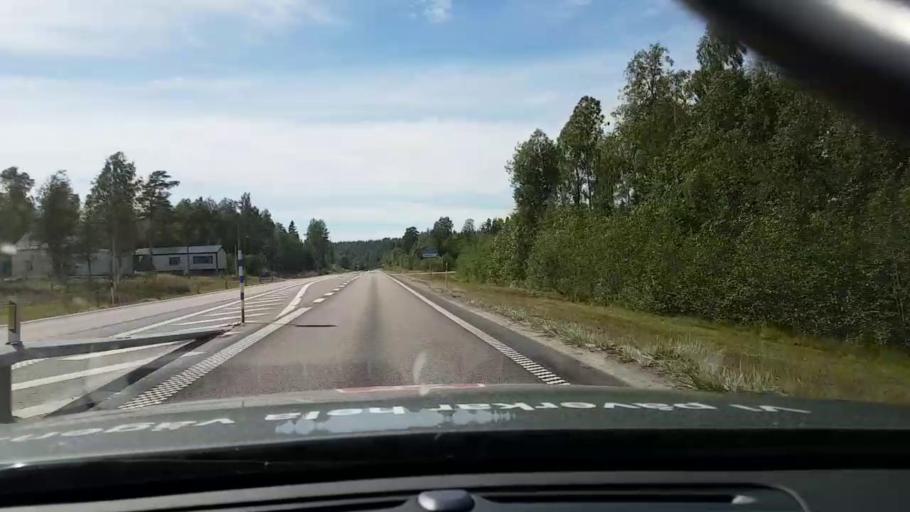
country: SE
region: Vaesternorrland
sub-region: OErnskoeldsviks Kommun
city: Husum
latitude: 63.3453
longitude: 19.1272
